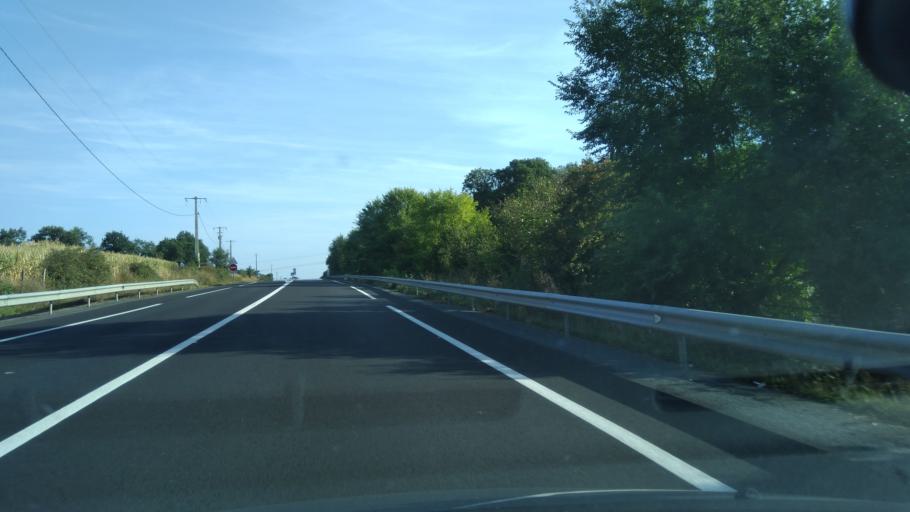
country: FR
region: Pays de la Loire
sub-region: Departement de la Mayenne
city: Entrammes
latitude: 47.9406
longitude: -0.6970
